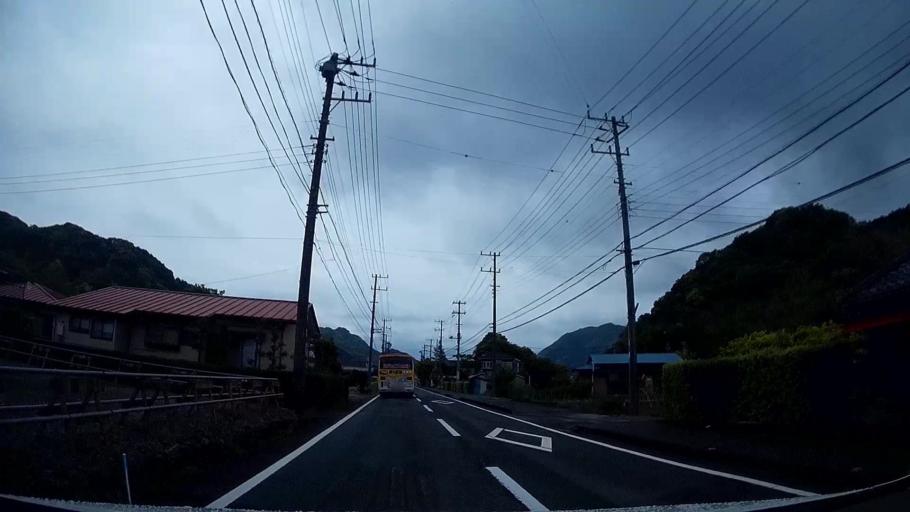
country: JP
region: Shizuoka
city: Shimoda
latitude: 34.7633
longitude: 138.9797
